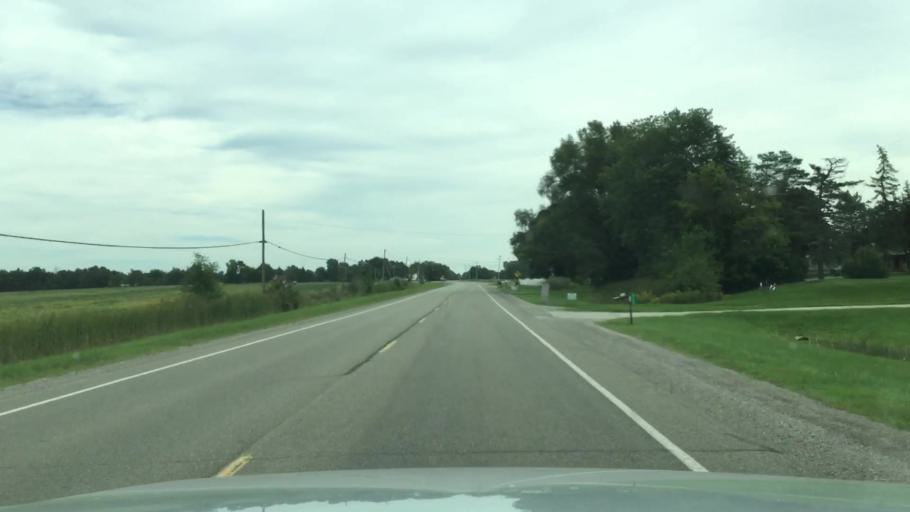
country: US
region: Michigan
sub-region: Shiawassee County
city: Durand
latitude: 42.9255
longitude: -83.9726
